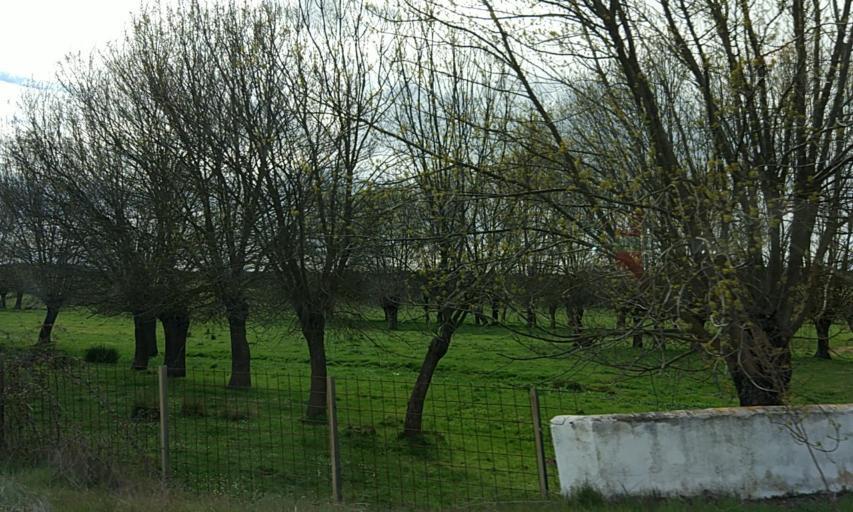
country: ES
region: Castille and Leon
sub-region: Provincia de Salamanca
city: Pastores
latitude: 40.5358
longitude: -6.5665
